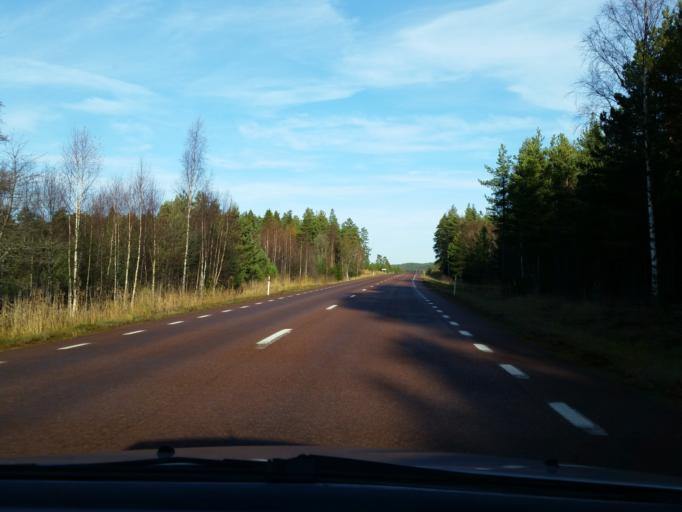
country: AX
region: Alands landsbygd
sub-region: Finstroem
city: Finstroem
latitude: 60.2841
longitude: 19.9527
